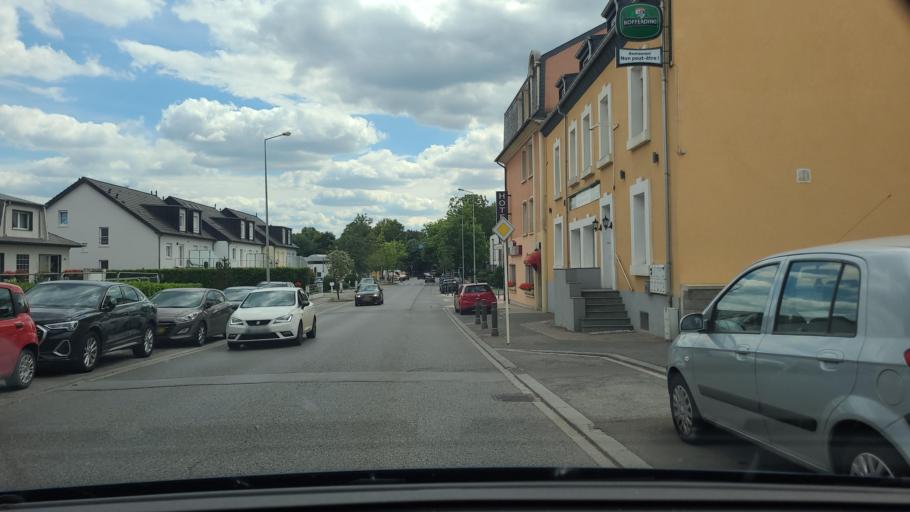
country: LU
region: Luxembourg
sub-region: Canton d'Esch-sur-Alzette
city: Bettembourg
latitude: 49.5269
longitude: 6.1012
